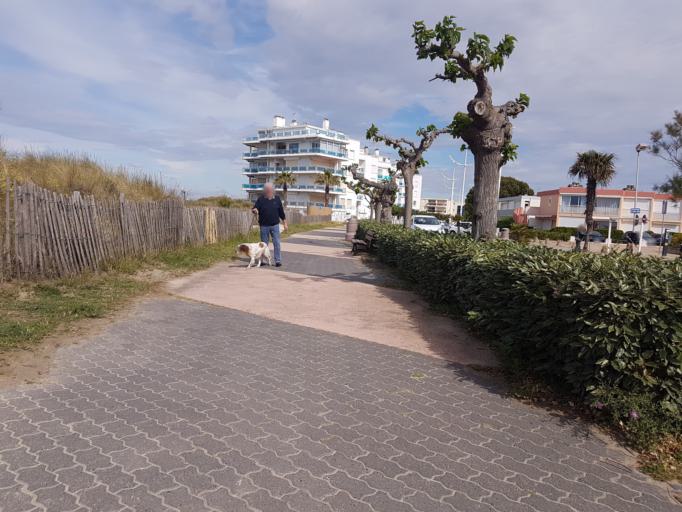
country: FR
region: Languedoc-Roussillon
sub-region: Departement du Gard
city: Le Grau-du-Roi
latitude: 43.5463
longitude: 4.1250
